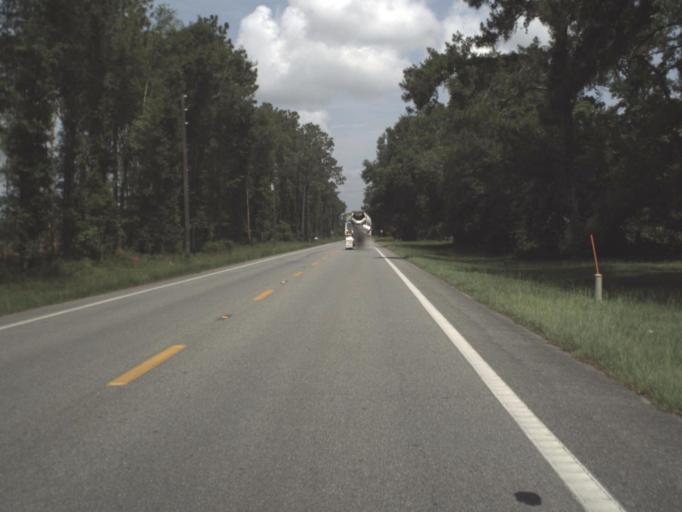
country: US
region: Florida
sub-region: Madison County
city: Madison
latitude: 30.4452
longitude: -83.3368
